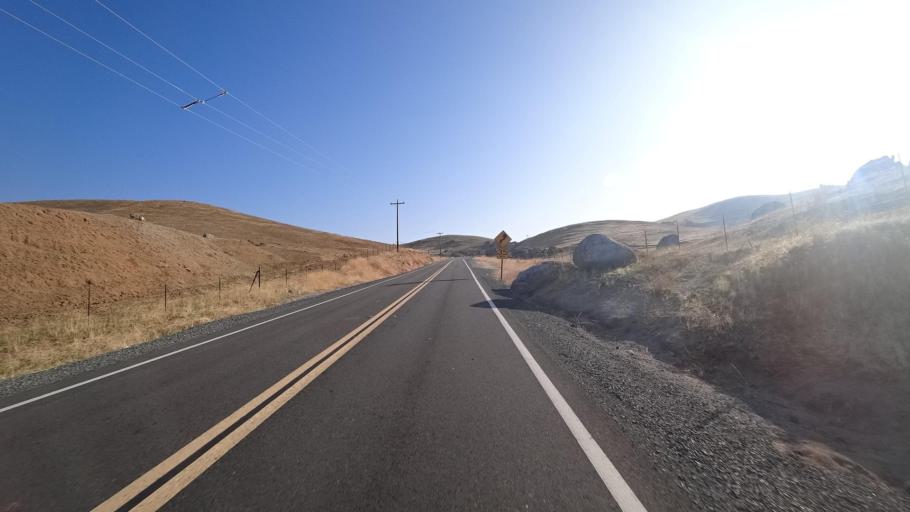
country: US
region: California
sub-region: Tulare County
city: Richgrove
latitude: 35.7426
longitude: -118.9025
